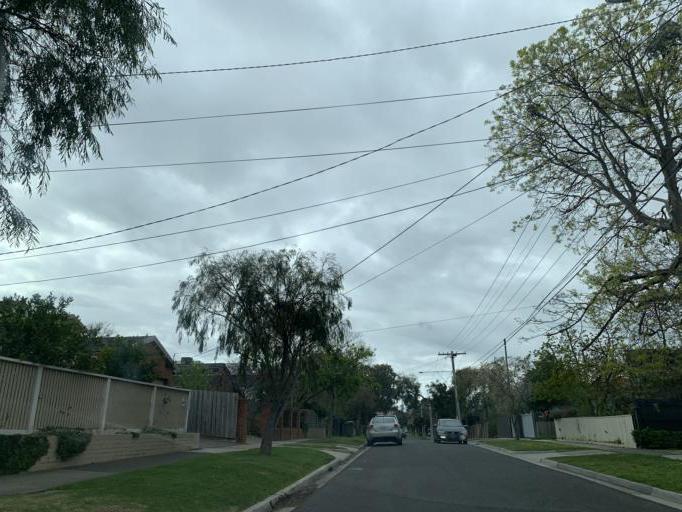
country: AU
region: Victoria
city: Beaumaris
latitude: -37.9887
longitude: 145.0406
